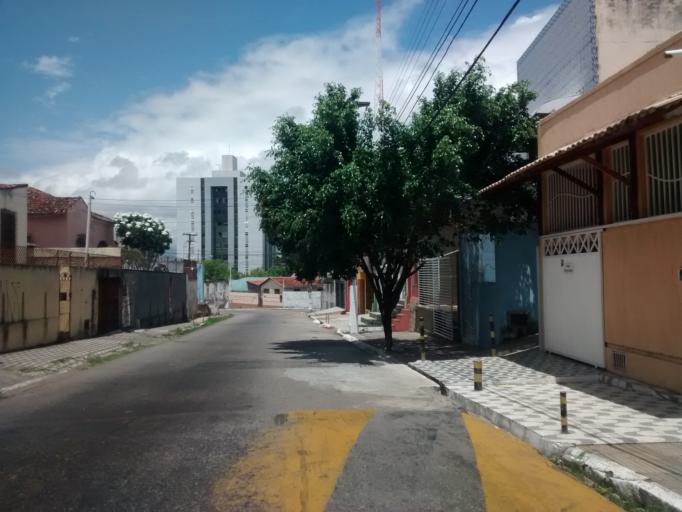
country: BR
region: Rio Grande do Norte
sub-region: Natal
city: Natal
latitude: -5.7876
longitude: -35.2102
